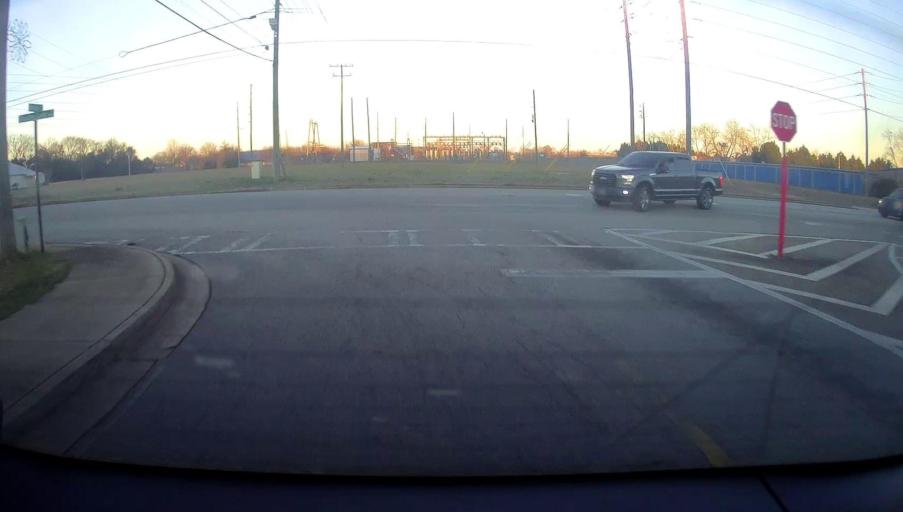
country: US
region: Georgia
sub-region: Houston County
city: Centerville
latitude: 32.6317
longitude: -83.6919
